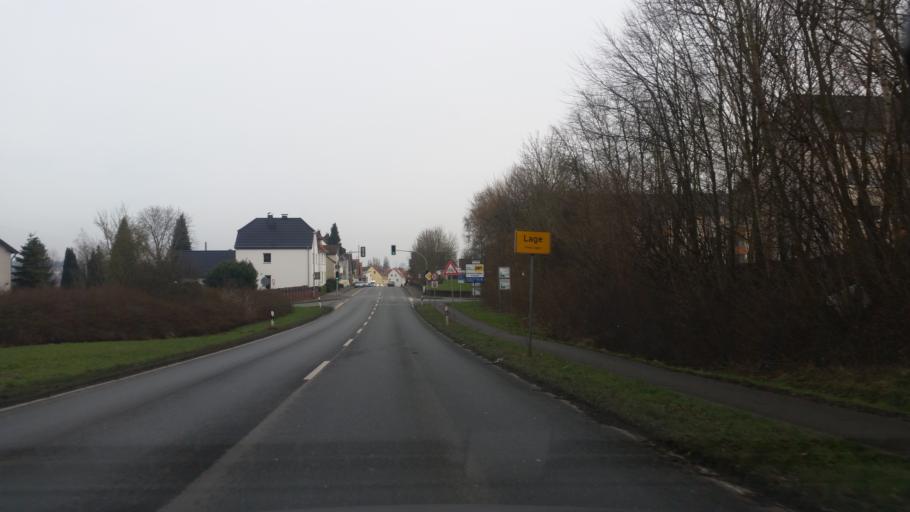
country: DE
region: North Rhine-Westphalia
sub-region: Regierungsbezirk Detmold
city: Lage
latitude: 51.9888
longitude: 8.7789
